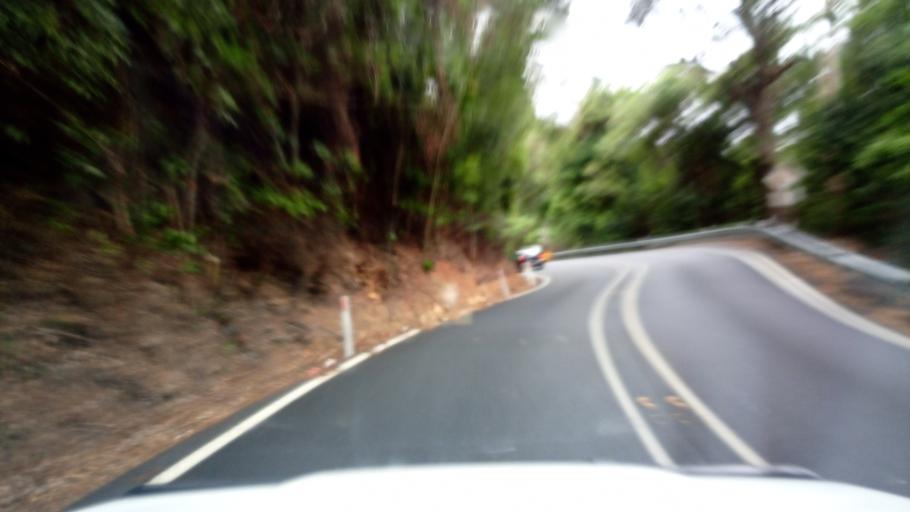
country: AU
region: Queensland
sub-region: Tablelands
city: Kuranda
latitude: -16.8404
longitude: 145.6721
